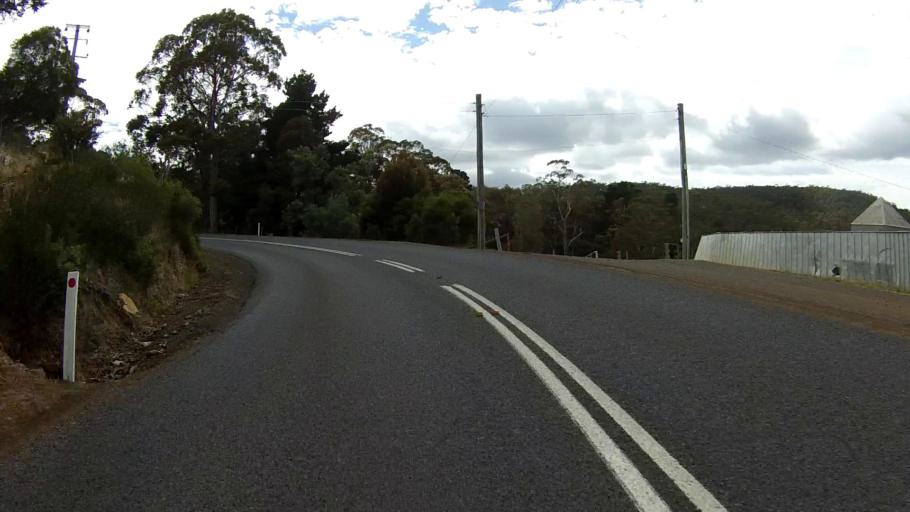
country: AU
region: Tasmania
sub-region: Clarence
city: Lindisfarne
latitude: -42.7828
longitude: 147.3591
